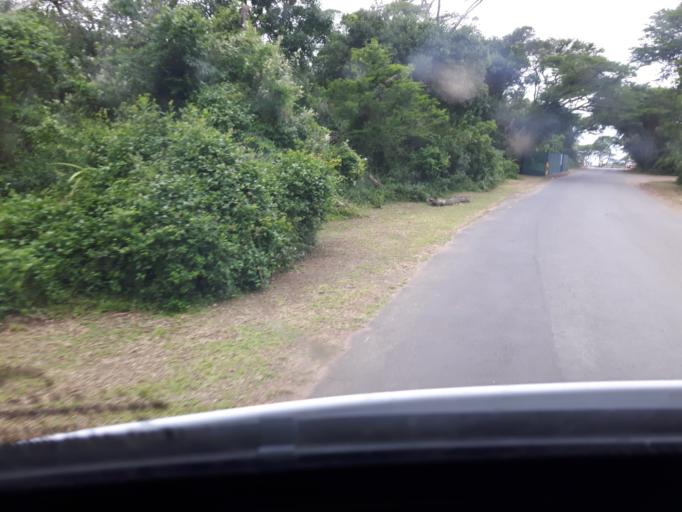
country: ZA
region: KwaZulu-Natal
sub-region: uMkhanyakude District Municipality
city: Mtubatuba
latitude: -28.3834
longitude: 32.4169
